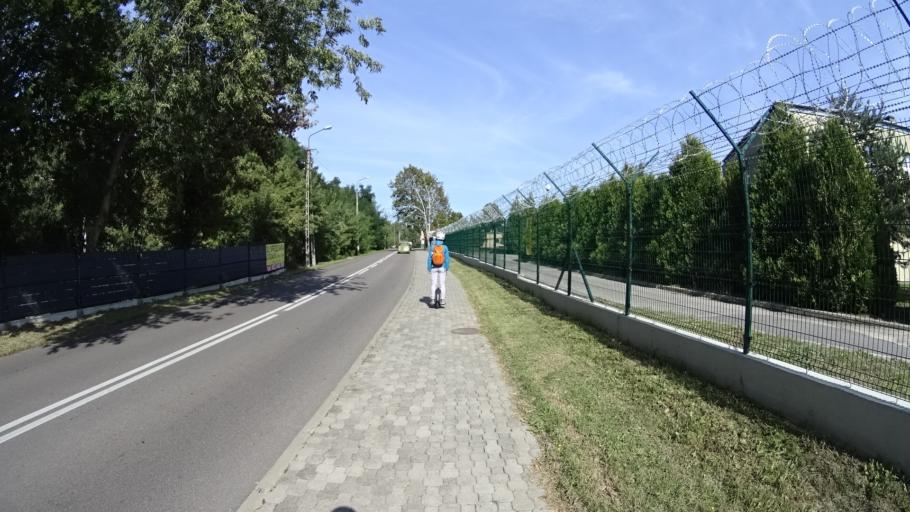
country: PL
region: Masovian Voivodeship
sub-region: Powiat legionowski
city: Bialobrzegi
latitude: 52.4439
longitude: 21.0560
